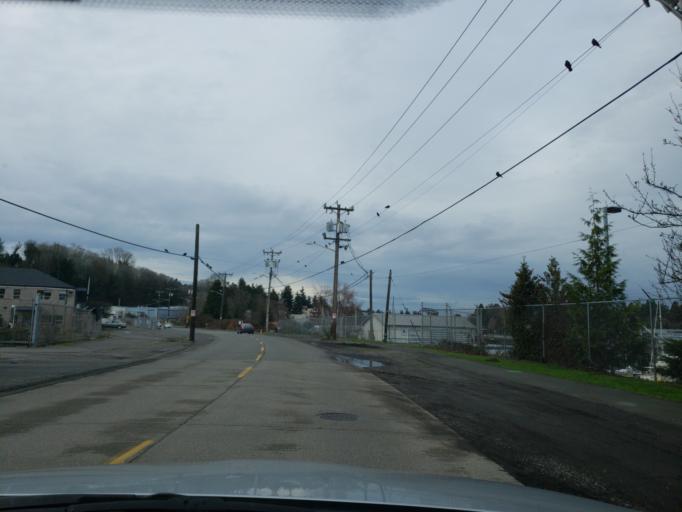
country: US
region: Washington
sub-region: King County
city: Seattle
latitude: 47.6625
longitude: -122.3917
